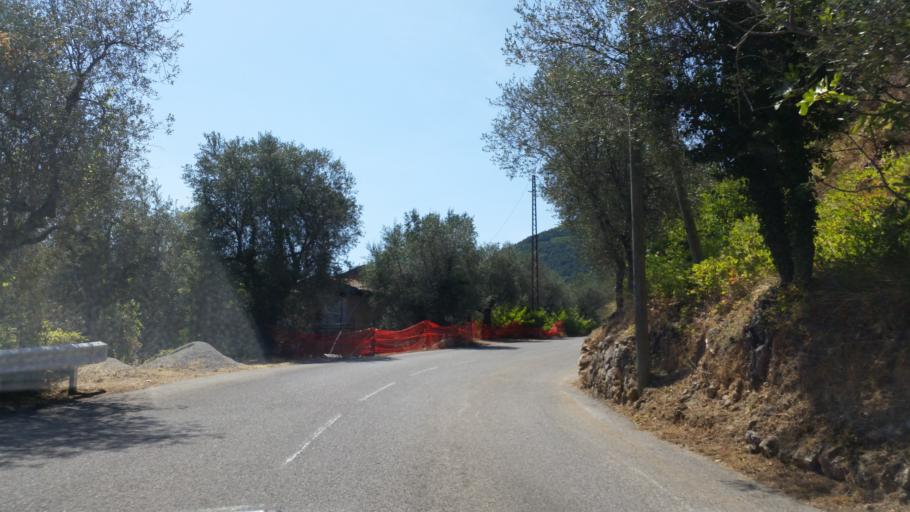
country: FR
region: Provence-Alpes-Cote d'Azur
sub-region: Departement des Alpes-Maritimes
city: Breil-sur-Roya
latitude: 43.9466
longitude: 7.5112
